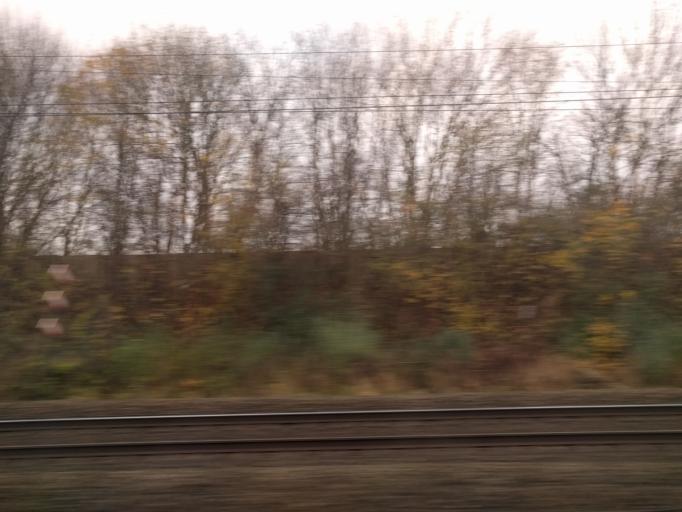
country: DK
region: Capital Region
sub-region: Hoje-Taastrup Kommune
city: Flong
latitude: 55.6503
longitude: 12.1844
